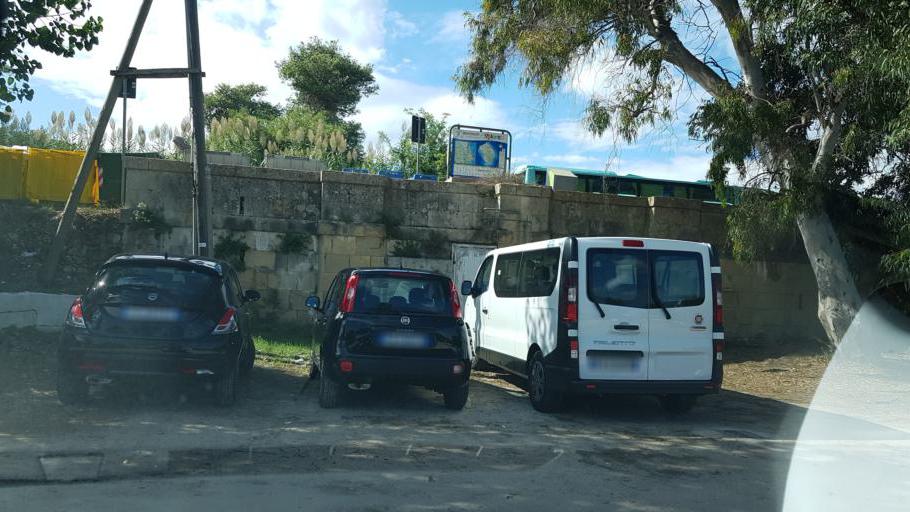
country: IT
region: Apulia
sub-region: Provincia di Lecce
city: Otranto
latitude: 40.2034
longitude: 18.4575
